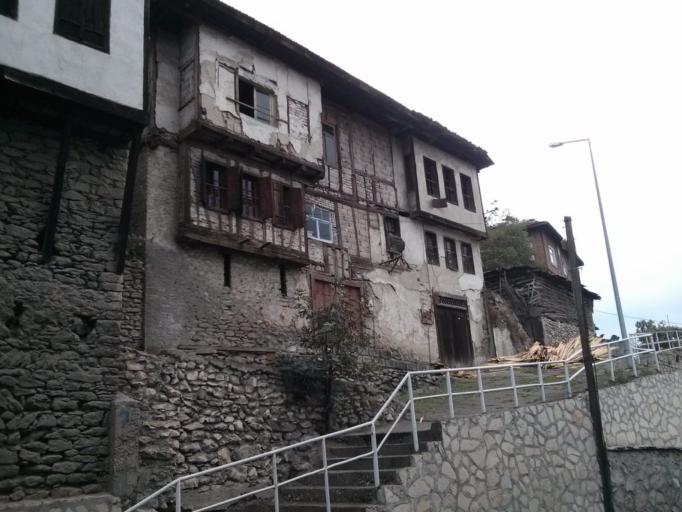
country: TR
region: Karabuk
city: Safranbolu
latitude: 41.2462
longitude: 32.6932
